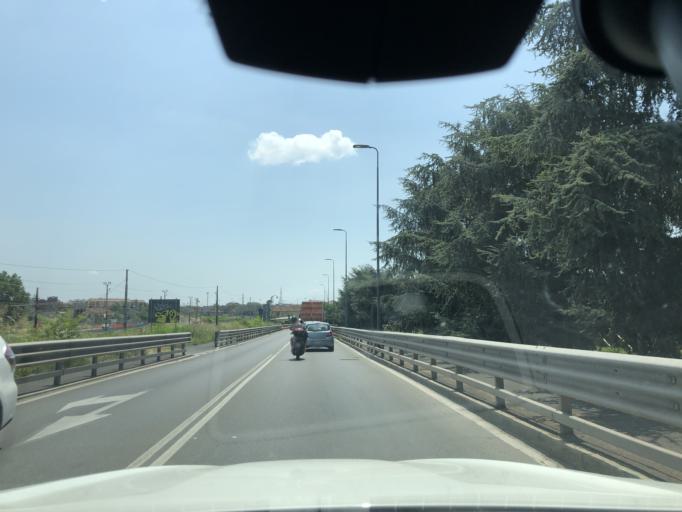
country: IT
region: Lombardy
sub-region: Citta metropolitana di Milano
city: Sesto San Giovanni
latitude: 45.5063
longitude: 9.2113
